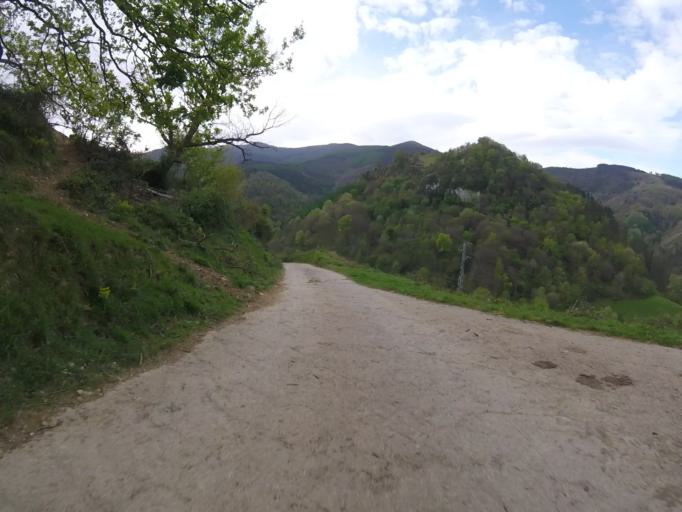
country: ES
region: Basque Country
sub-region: Provincia de Guipuzcoa
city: Aya
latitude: 43.2077
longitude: -2.1770
